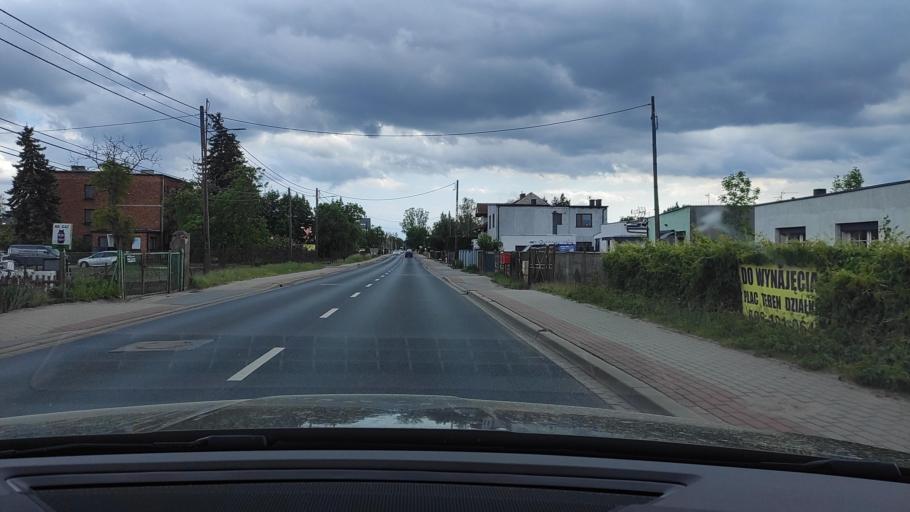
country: PL
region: Greater Poland Voivodeship
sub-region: Powiat poznanski
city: Swarzedz
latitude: 52.3926
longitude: 17.0762
